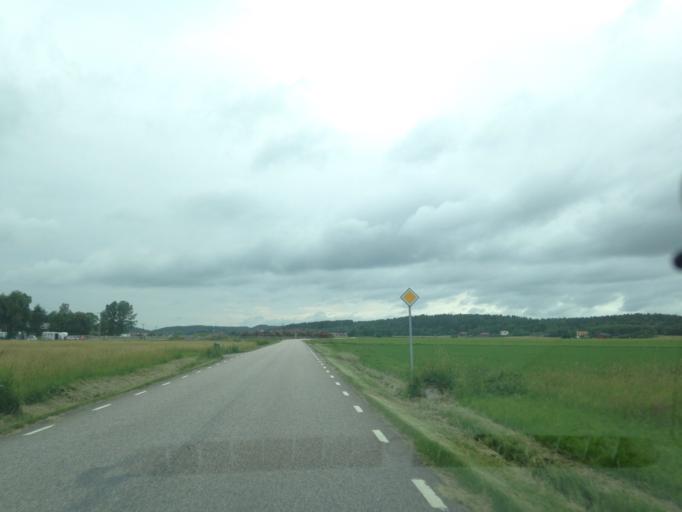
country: SE
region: Vaestra Goetaland
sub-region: Goteborg
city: Torslanda
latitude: 57.8245
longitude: 11.8207
